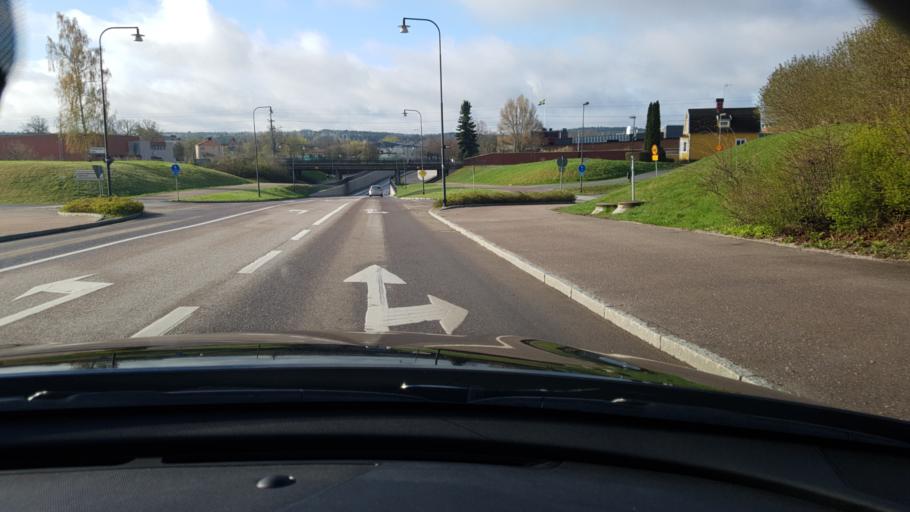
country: SE
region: Vaestmanland
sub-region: Arboga Kommun
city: Arboga
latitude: 59.3989
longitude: 15.8326
